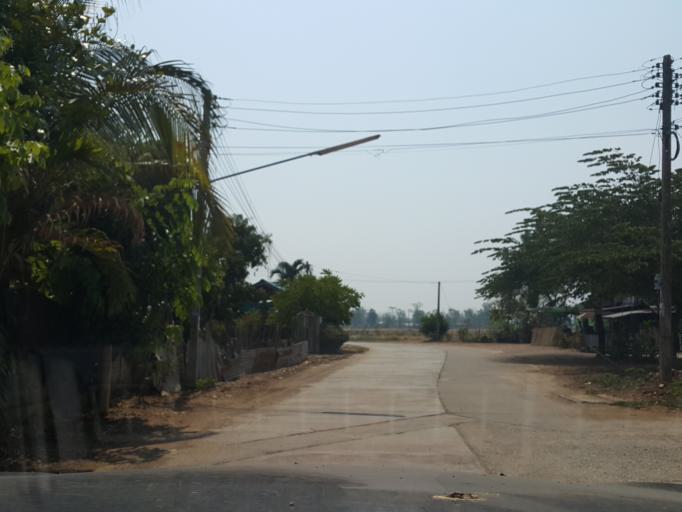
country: TH
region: Sukhothai
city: Thung Saliam
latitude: 17.3122
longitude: 99.5563
